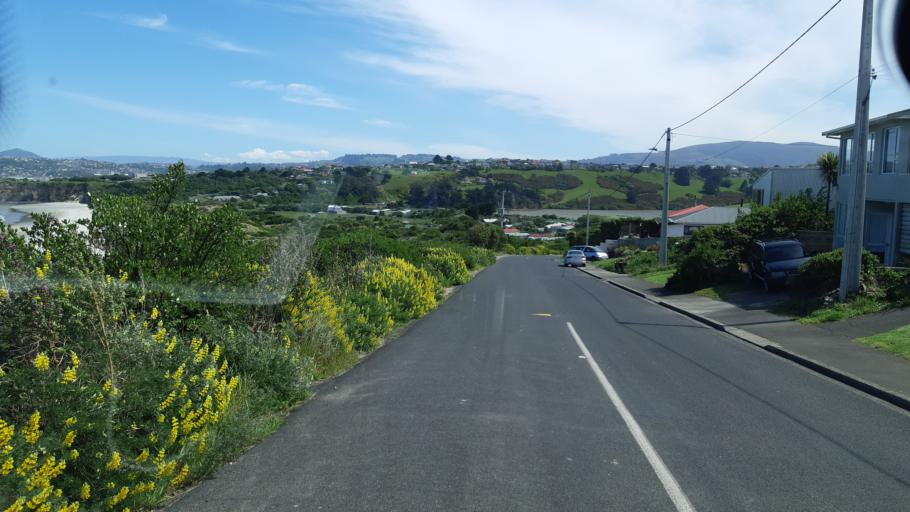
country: NZ
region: Otago
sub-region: Dunedin City
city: Dunedin
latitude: -45.9069
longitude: 170.5529
